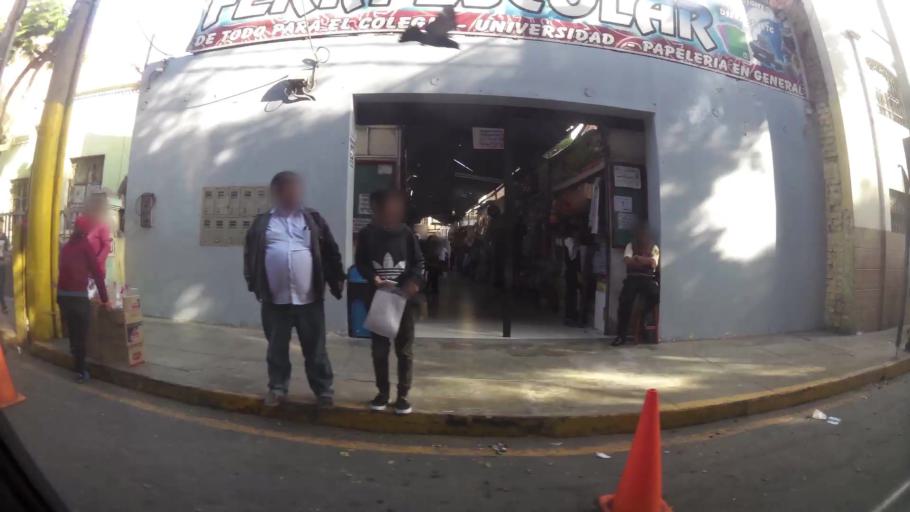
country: PE
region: Lima
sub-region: Huaura
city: Huacho
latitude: -11.1082
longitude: -77.6096
